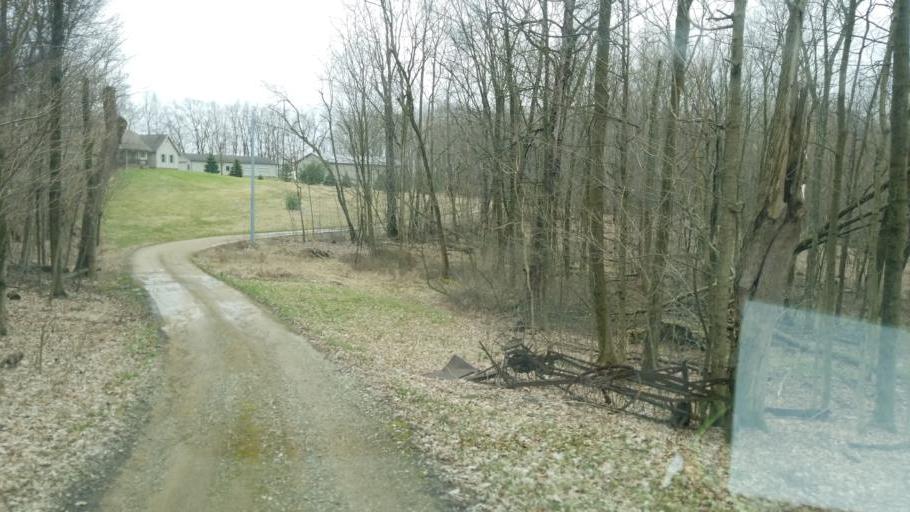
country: US
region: Ohio
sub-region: Knox County
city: Mount Vernon
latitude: 40.4588
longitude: -82.4323
